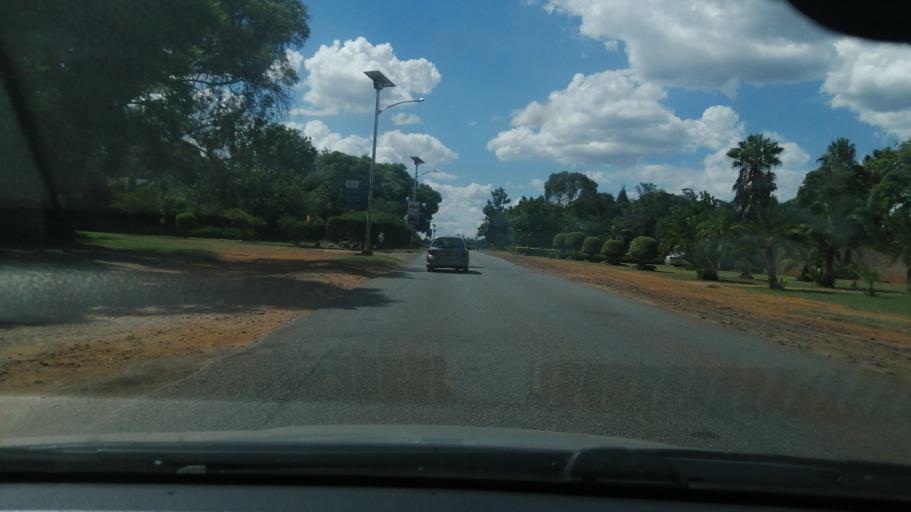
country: ZW
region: Harare
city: Harare
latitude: -17.7942
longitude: 31.0681
